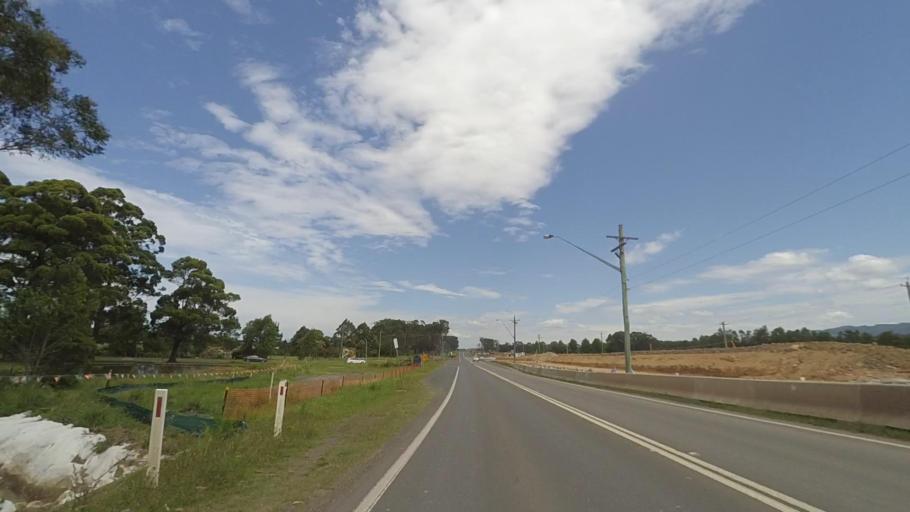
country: AU
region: New South Wales
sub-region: Shoalhaven Shire
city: Berry
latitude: -34.7750
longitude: 150.6850
